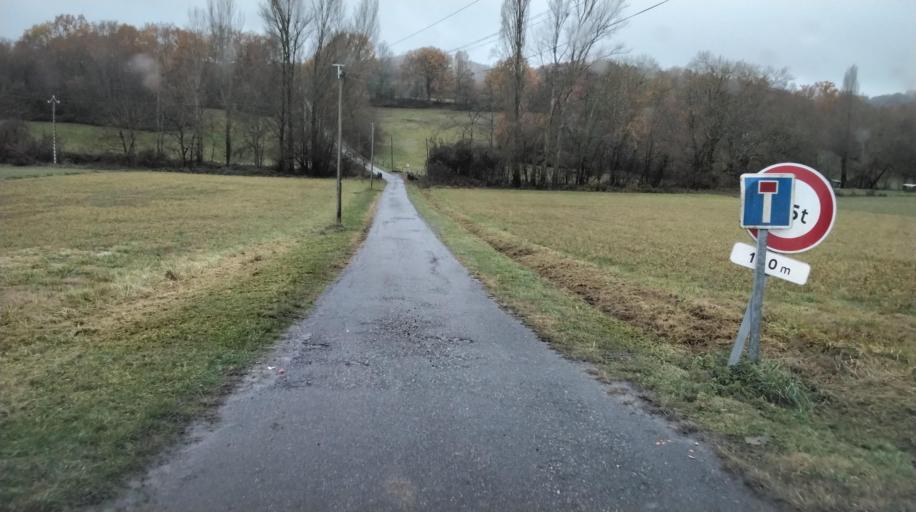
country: FR
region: Midi-Pyrenees
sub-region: Departement de la Haute-Garonne
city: Cazeres
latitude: 43.1684
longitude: 1.1450
